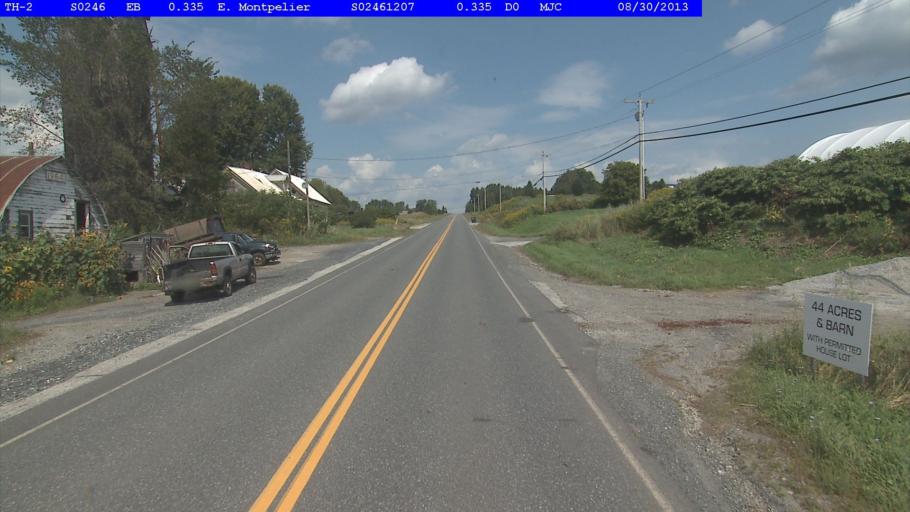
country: US
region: Vermont
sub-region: Washington County
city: Montpelier
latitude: 44.2569
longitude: -72.5169
